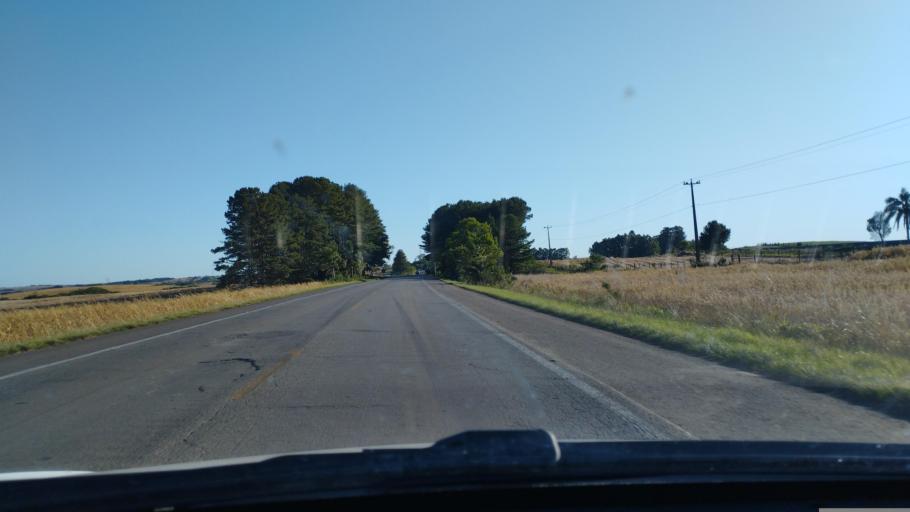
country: BR
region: Rio Grande do Sul
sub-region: Julio De Castilhos
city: Julio de Castilhos
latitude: -29.4335
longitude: -53.6762
